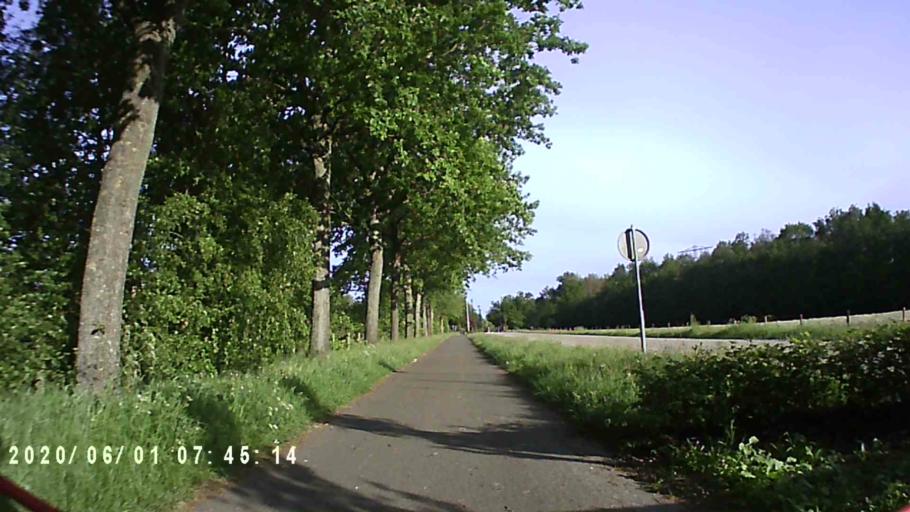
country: NL
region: Friesland
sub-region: Gemeente Dantumadiel
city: Rinsumageast
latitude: 53.2927
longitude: 5.9636
